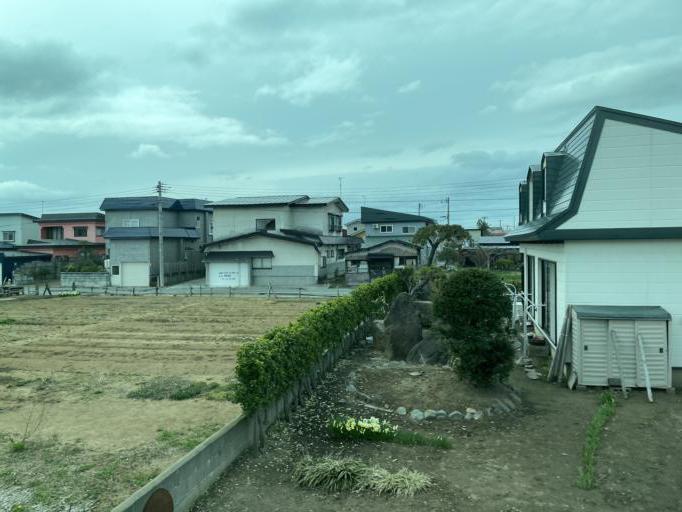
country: JP
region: Aomori
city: Goshogawara
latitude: 40.7549
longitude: 140.4348
